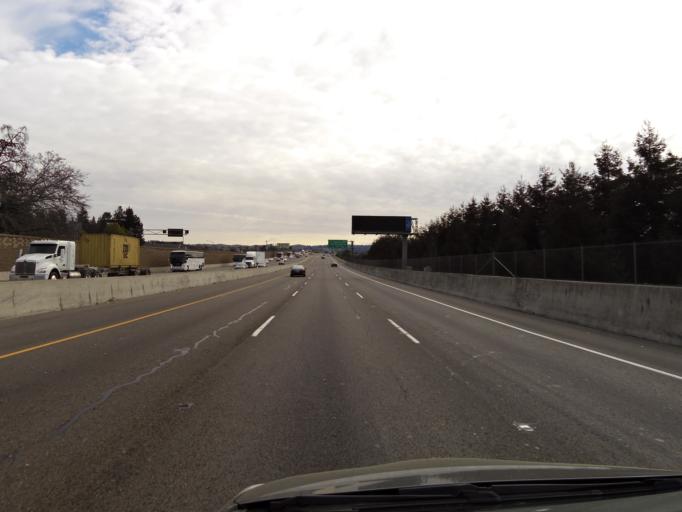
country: US
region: California
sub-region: Alameda County
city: San Lorenzo
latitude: 37.6902
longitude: -122.1237
